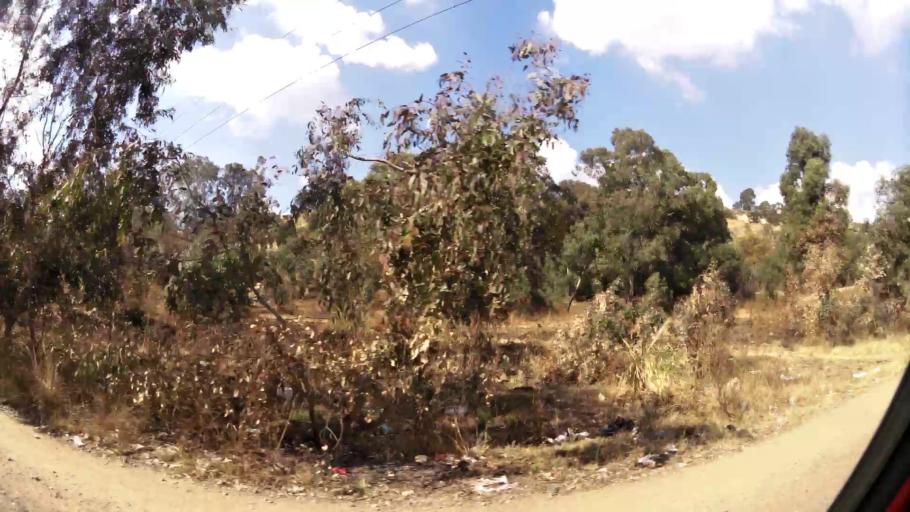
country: ZA
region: Gauteng
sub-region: City of Johannesburg Metropolitan Municipality
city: Roodepoort
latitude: -26.1812
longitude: 27.8699
